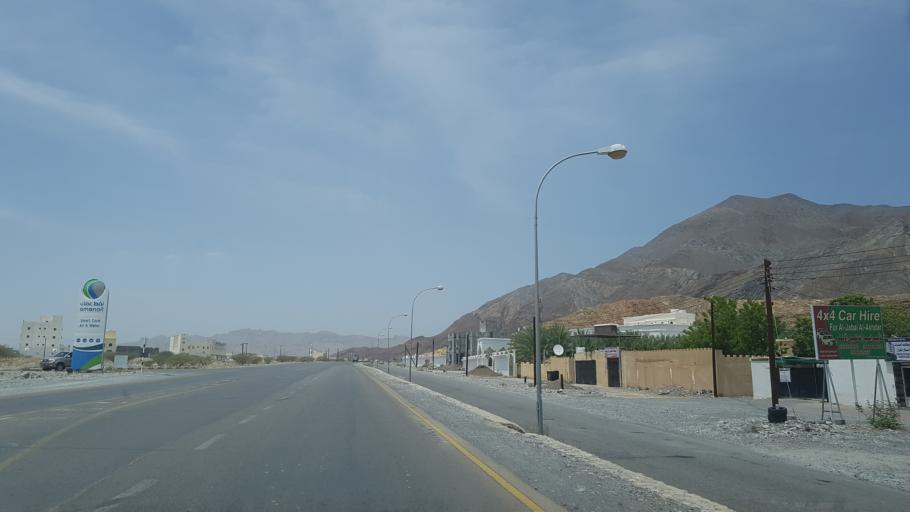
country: OM
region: Muhafazat ad Dakhiliyah
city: Izki
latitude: 22.9181
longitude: 57.6691
